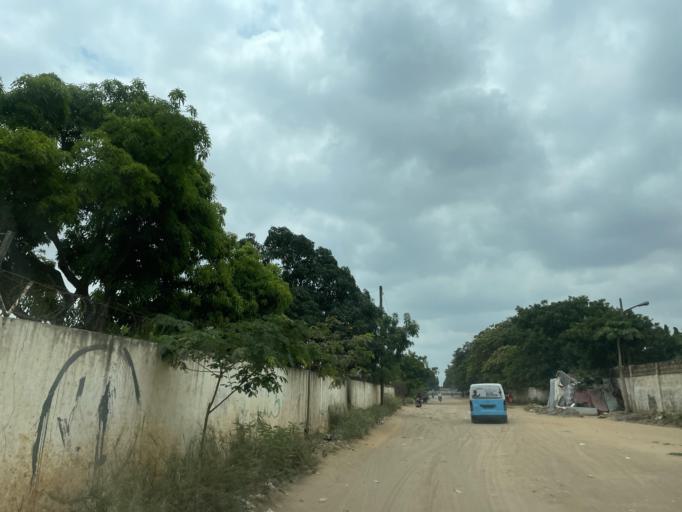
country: AO
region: Luanda
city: Luanda
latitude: -8.9107
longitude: 13.3790
